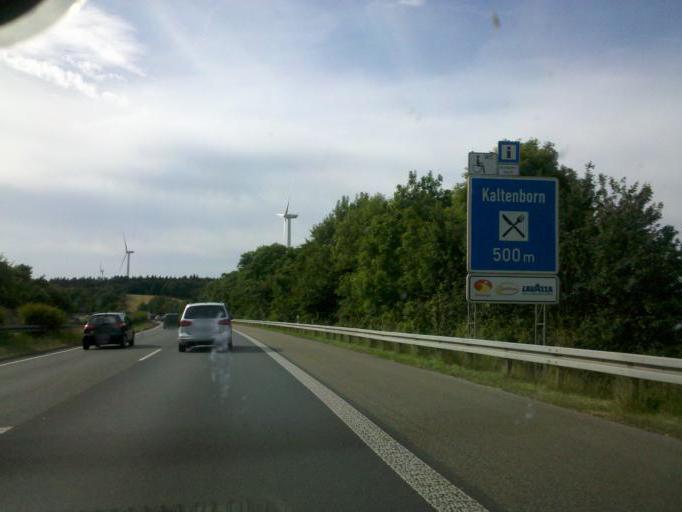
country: DE
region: North Rhine-Westphalia
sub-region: Regierungsbezirk Arnsberg
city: Nachrodt-Wiblingwerde
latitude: 51.2850
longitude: 7.5823
